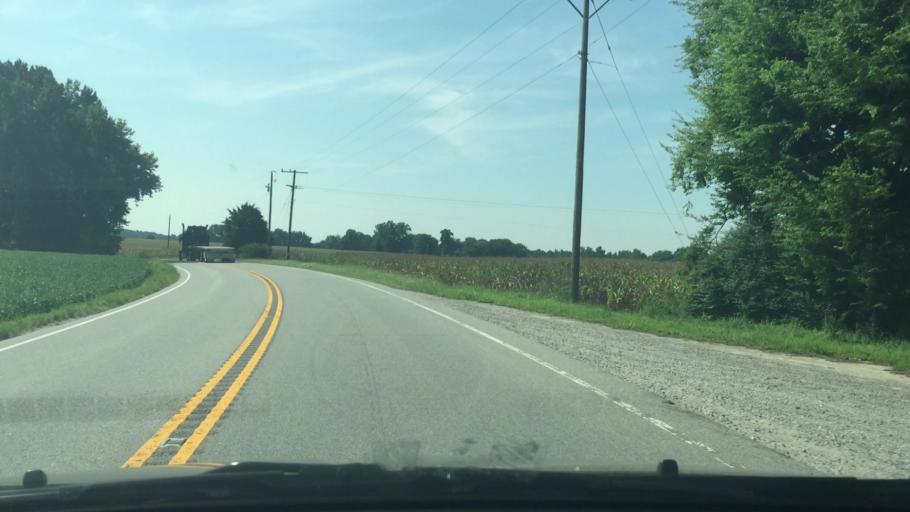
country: US
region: Virginia
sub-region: Sussex County
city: Sussex
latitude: 36.8853
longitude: -77.1546
